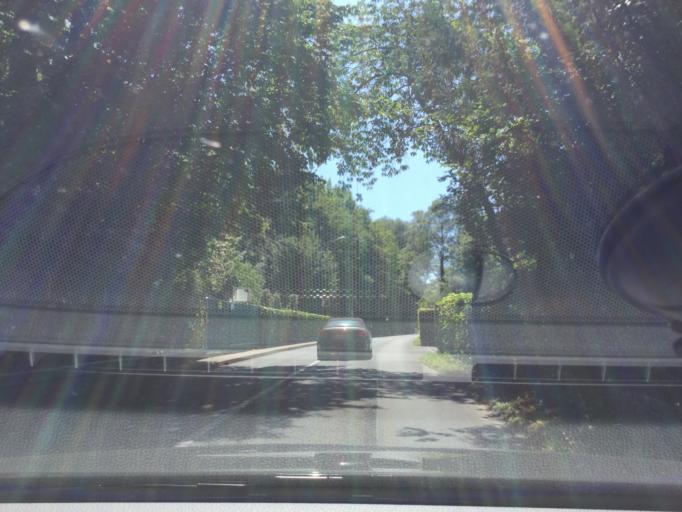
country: CH
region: Geneva
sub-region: Geneva
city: Corsier
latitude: 46.2675
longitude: 6.2171
